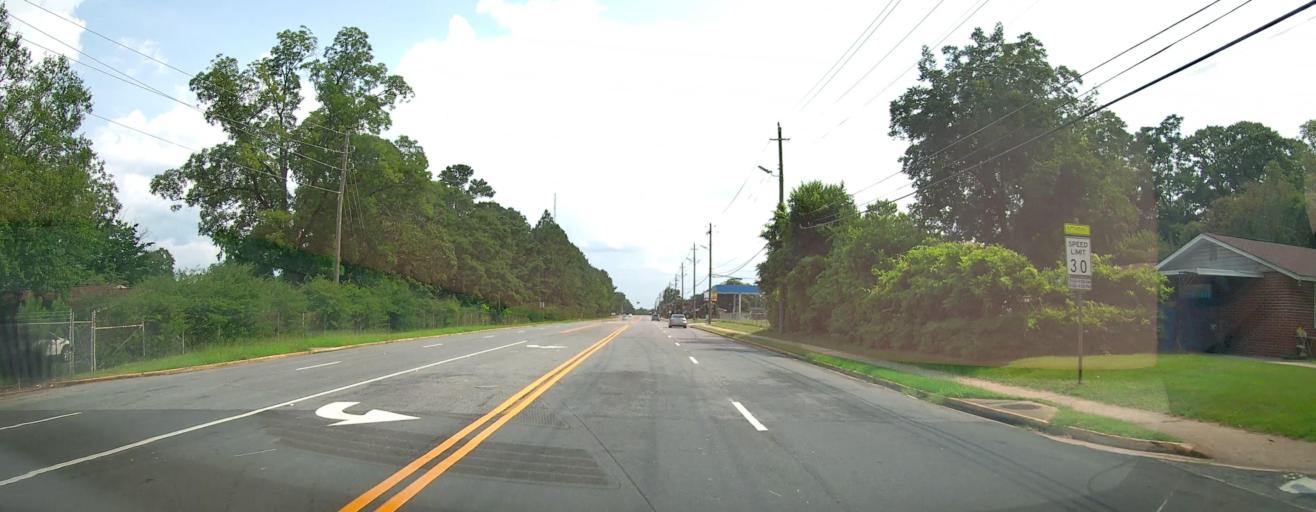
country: US
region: Georgia
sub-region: Houston County
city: Warner Robins
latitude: 32.6073
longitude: -83.6131
